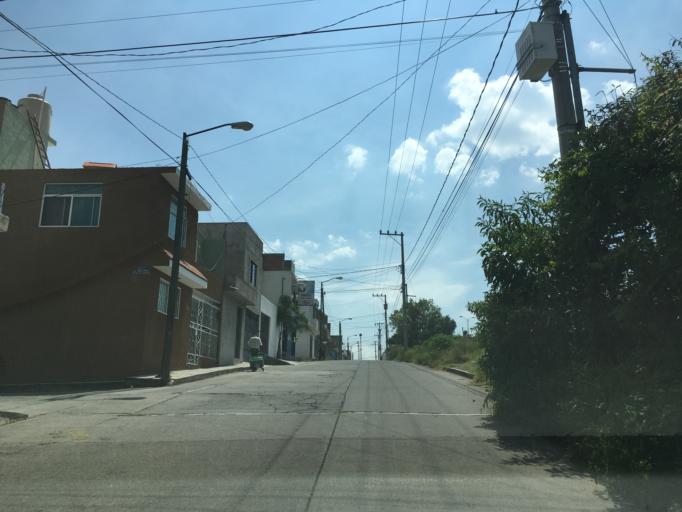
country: MX
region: Michoacan
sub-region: Morelia
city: Montana Monarca (Punta Altozano)
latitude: 19.6625
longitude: -101.1963
